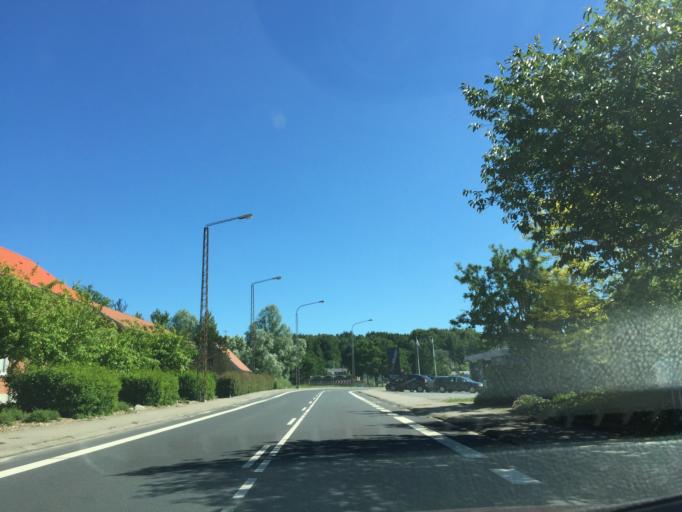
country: DK
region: Central Jutland
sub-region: Viborg Kommune
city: Bjerringbro
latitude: 56.3667
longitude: 9.6628
